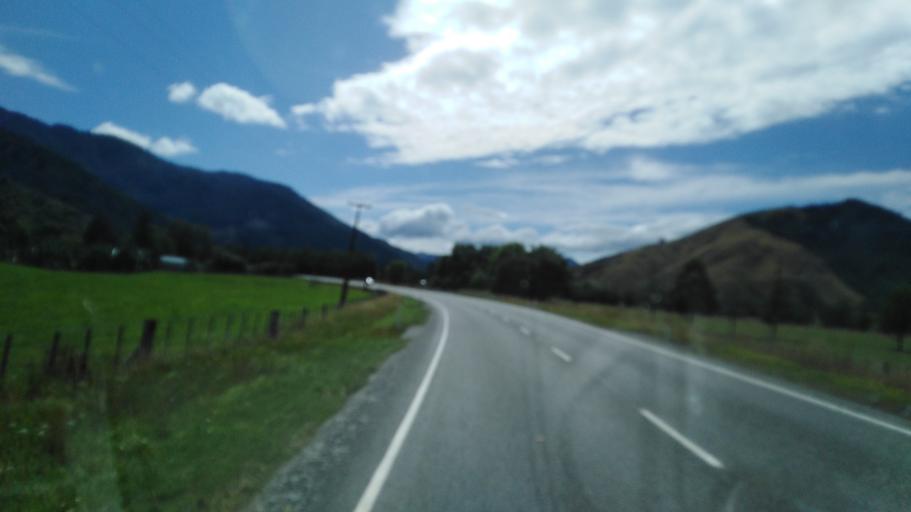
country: NZ
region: Marlborough
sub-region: Marlborough District
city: Picton
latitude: -41.3406
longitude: 173.7671
